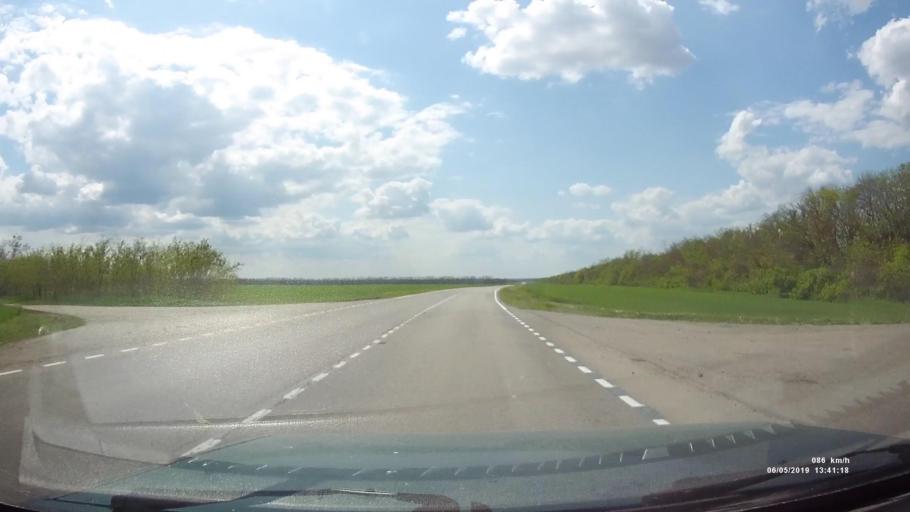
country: RU
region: Rostov
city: Ust'-Donetskiy
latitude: 47.6621
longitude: 40.6781
